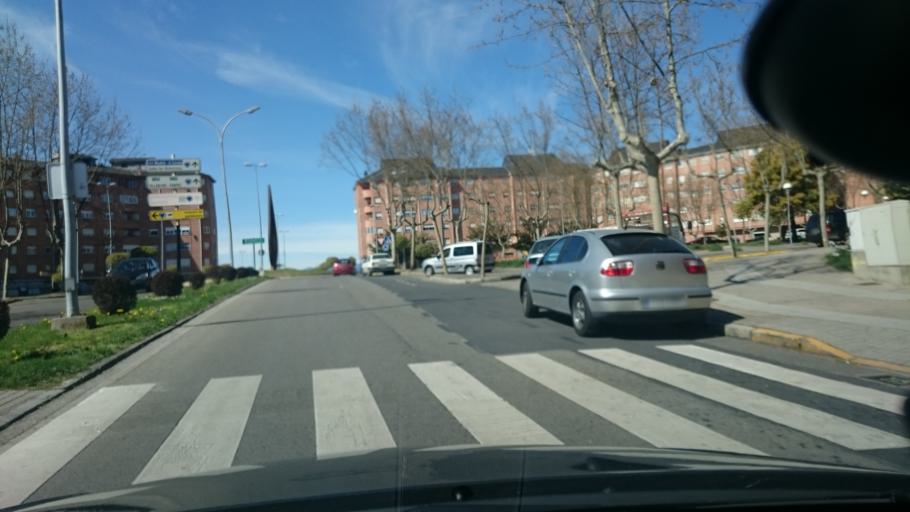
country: ES
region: Castille and Leon
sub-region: Provincia de Leon
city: Ponferrada
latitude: 42.5550
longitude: -6.5943
